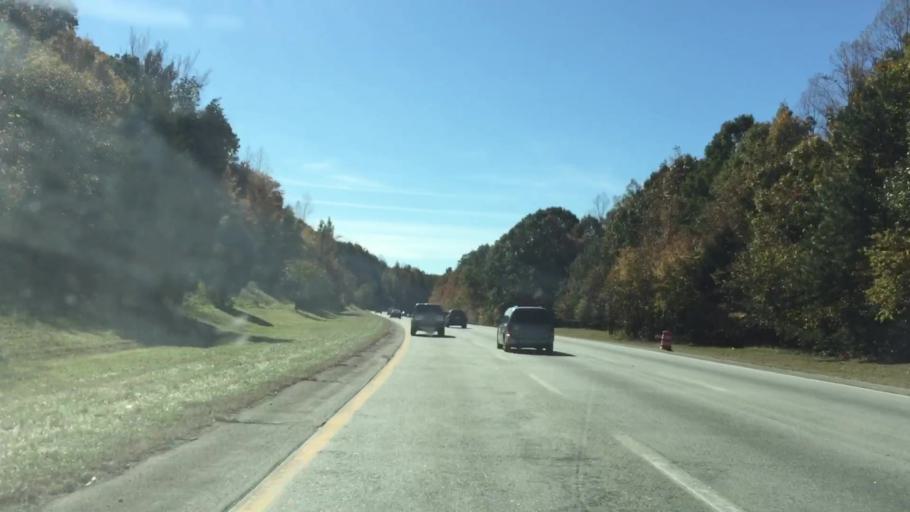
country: US
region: North Carolina
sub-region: Davidson County
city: Thomasville
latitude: 35.8316
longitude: -80.1469
